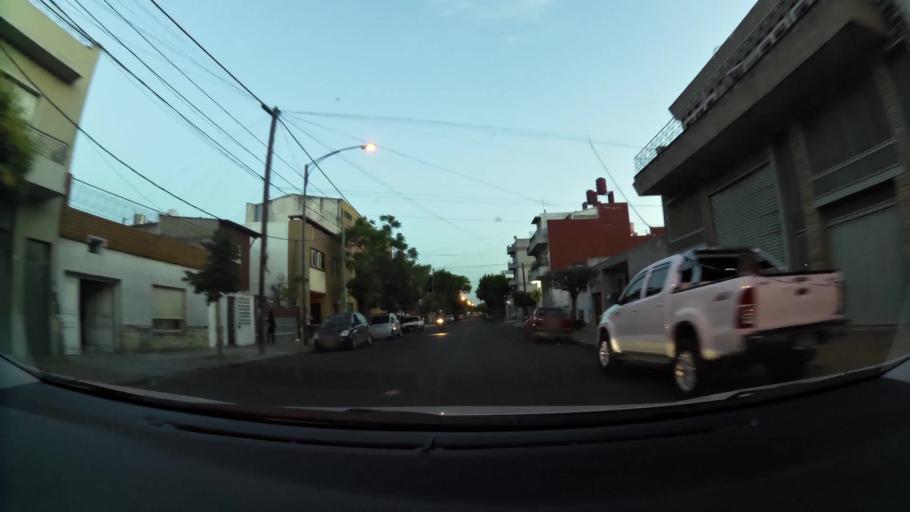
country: AR
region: Buenos Aires F.D.
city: Villa Lugano
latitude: -34.6904
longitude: -58.4683
